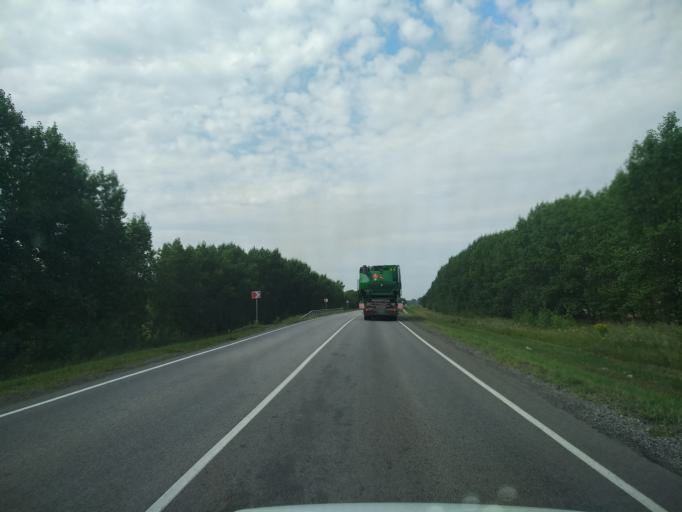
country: RU
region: Voronezj
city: Pereleshinskiy
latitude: 51.8764
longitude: 40.4102
